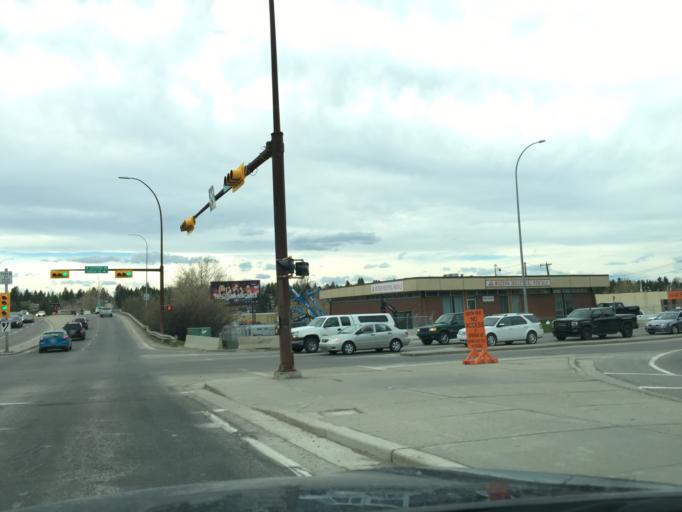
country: CA
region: Alberta
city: Calgary
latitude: 50.9651
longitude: -114.0743
